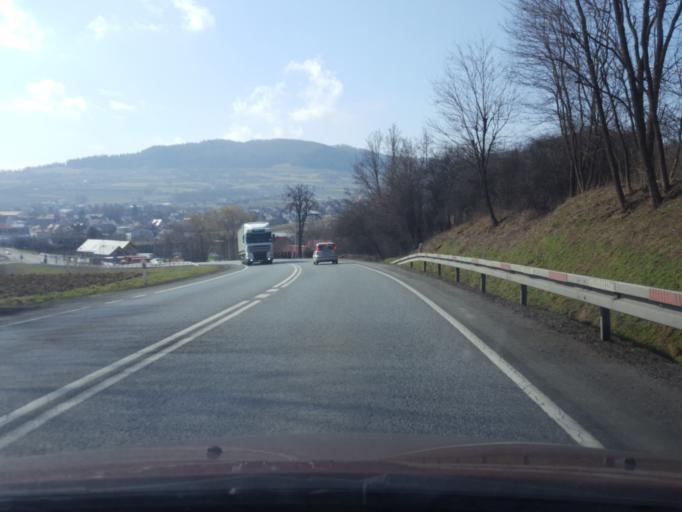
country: PL
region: Lesser Poland Voivodeship
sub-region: Powiat nowosadecki
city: Lososina Dolna
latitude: 49.7164
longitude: 20.6408
